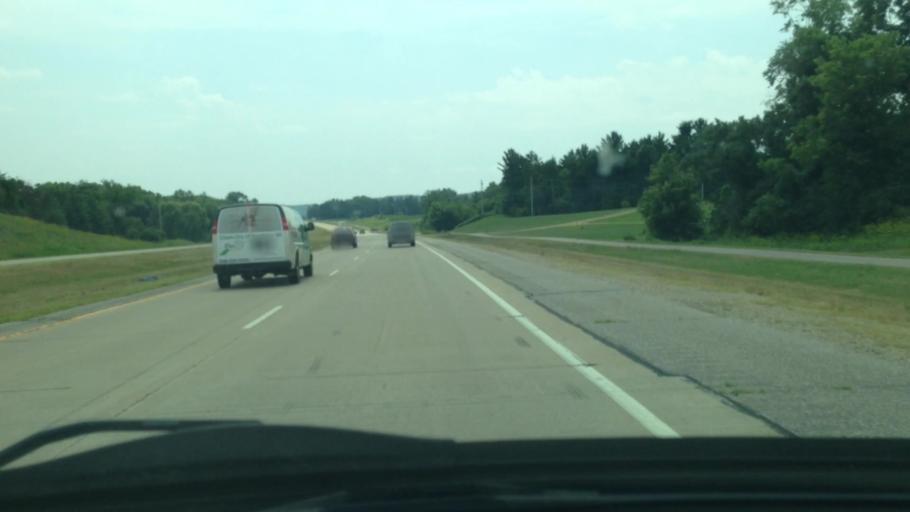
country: US
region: Wisconsin
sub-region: Sauk County
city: Sauk City
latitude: 43.2576
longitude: -89.7084
